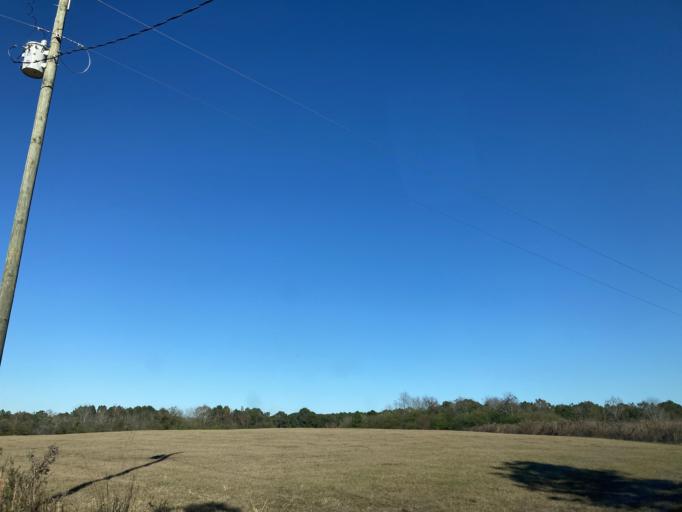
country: US
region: Mississippi
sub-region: Lamar County
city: Sumrall
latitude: 31.3355
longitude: -89.6192
